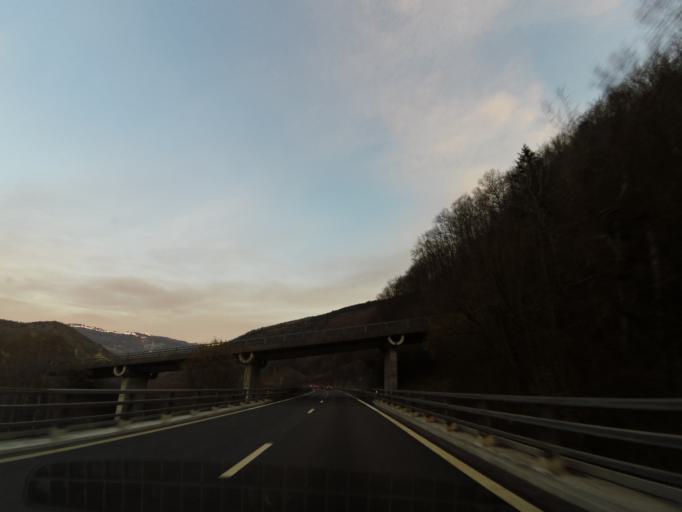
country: FR
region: Rhone-Alpes
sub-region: Departement de l'Ain
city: Chatillon-en-Michaille
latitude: 46.1652
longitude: 5.7555
